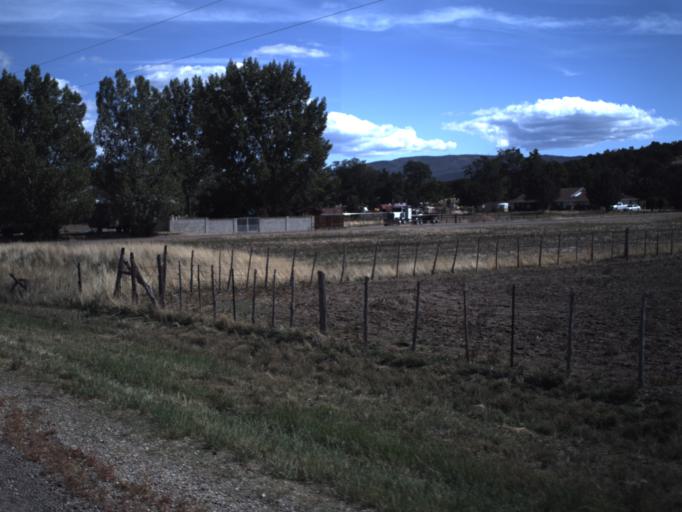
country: US
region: Utah
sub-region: Washington County
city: Enterprise
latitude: 37.5734
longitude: -113.7338
